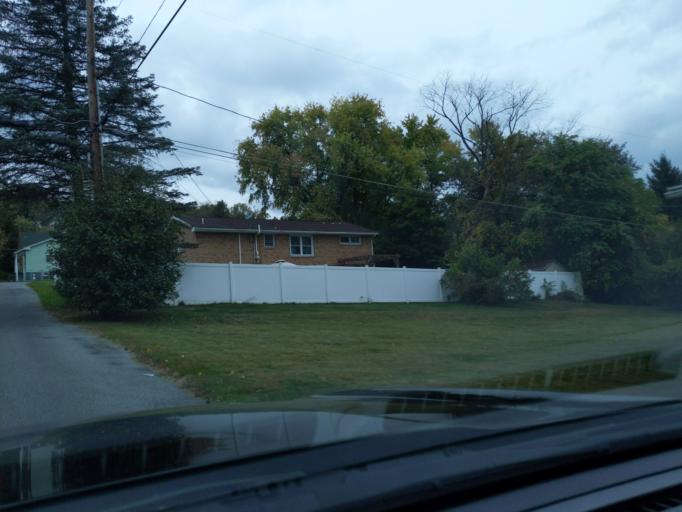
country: US
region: Pennsylvania
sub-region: Blair County
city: Altoona
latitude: 40.5079
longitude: -78.3865
